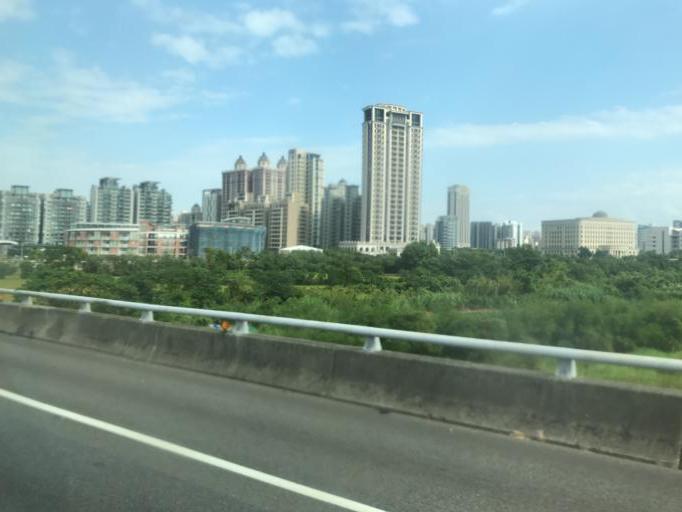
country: TW
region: Taiwan
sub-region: Hsinchu
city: Zhubei
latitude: 24.8138
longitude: 121.0120
